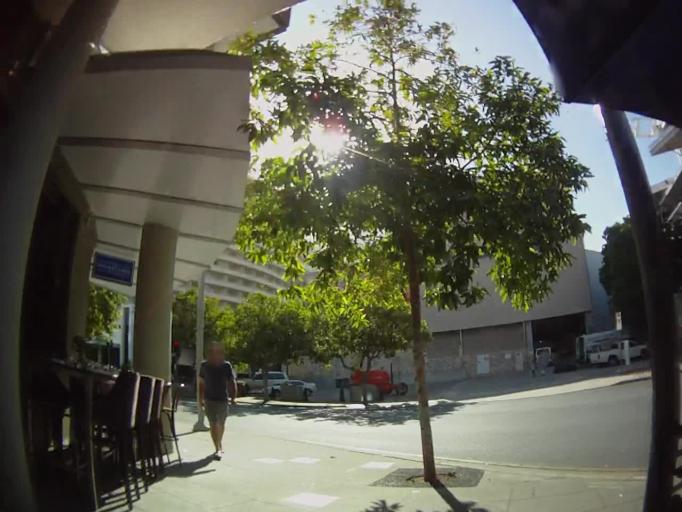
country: AU
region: Queensland
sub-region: Brisbane
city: South Brisbane
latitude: -27.4774
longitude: 153.0212
